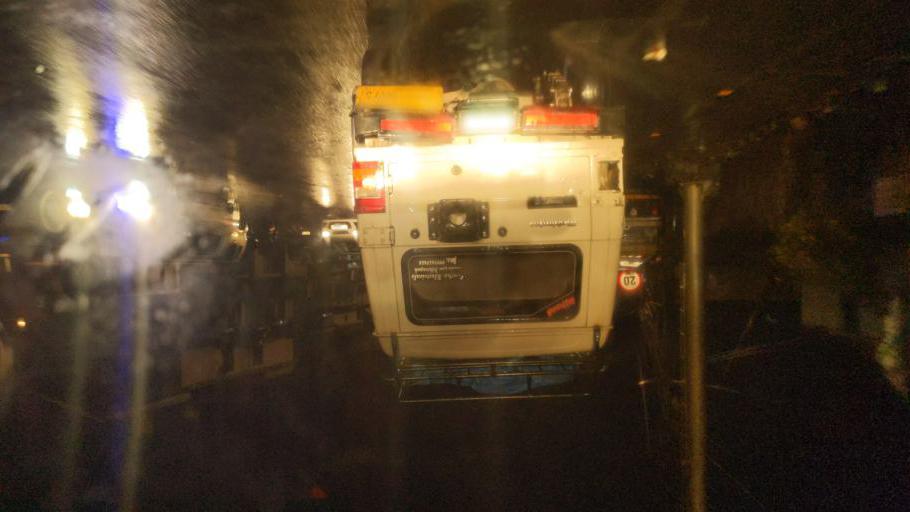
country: IN
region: Uttarakhand
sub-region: Naini Tal
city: Haldwani
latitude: 29.2715
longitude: 79.5442
